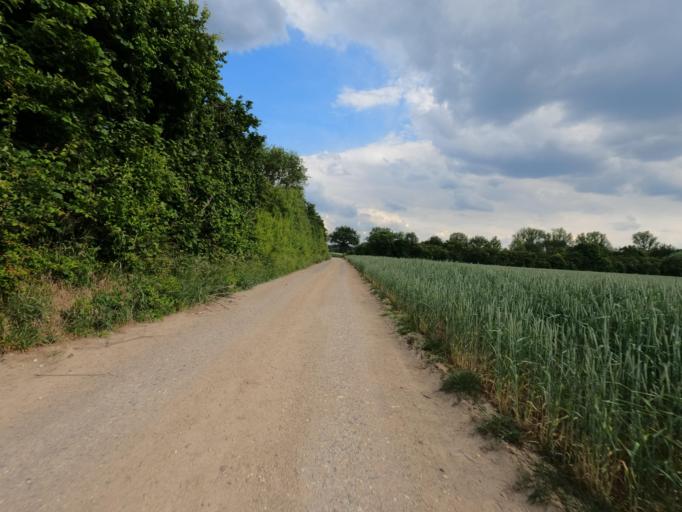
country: DE
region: North Rhine-Westphalia
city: Huckelhoven
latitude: 51.0778
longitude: 6.2085
